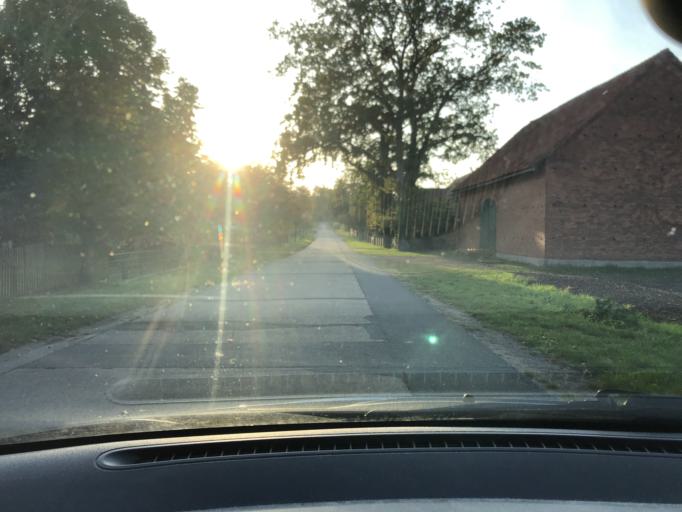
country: DE
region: Lower Saxony
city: Hitzacker
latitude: 53.1511
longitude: 10.9848
